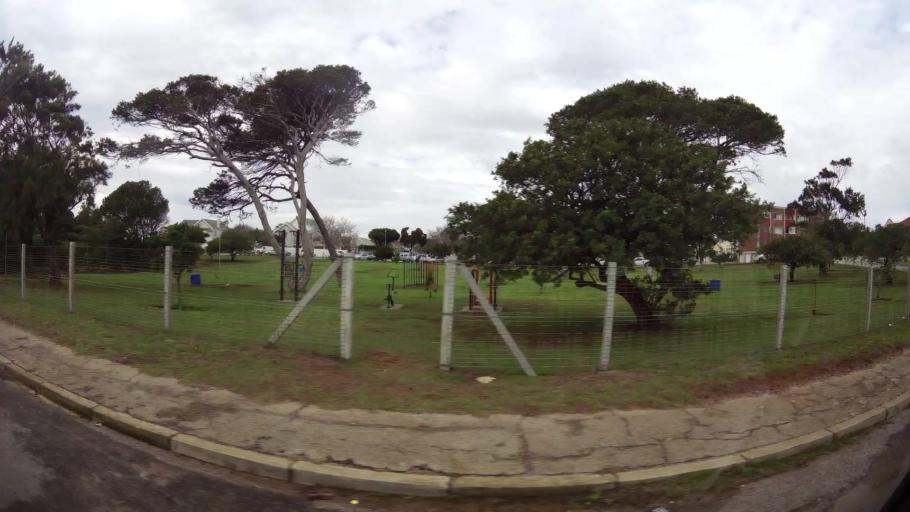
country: ZA
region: Eastern Cape
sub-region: Nelson Mandela Bay Metropolitan Municipality
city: Port Elizabeth
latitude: -33.9574
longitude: 25.6079
